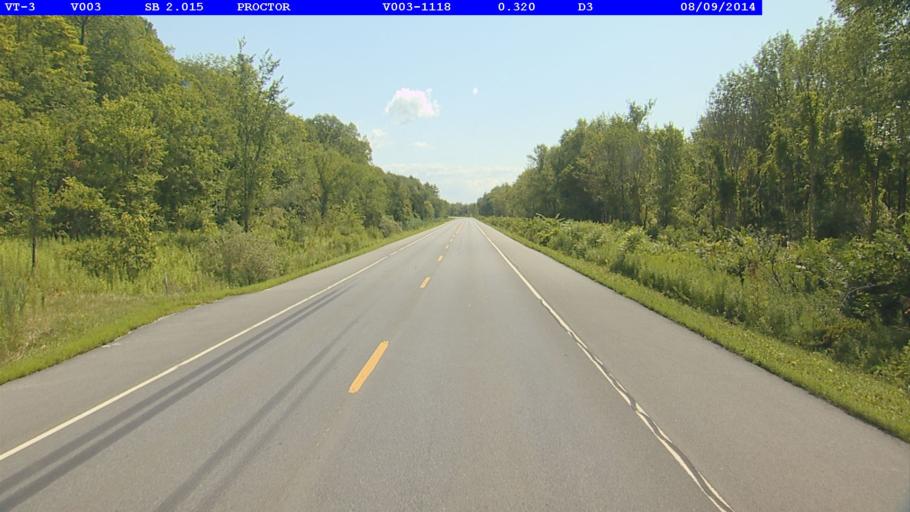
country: US
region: Vermont
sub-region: Rutland County
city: West Rutland
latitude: 43.6291
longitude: -73.0321
